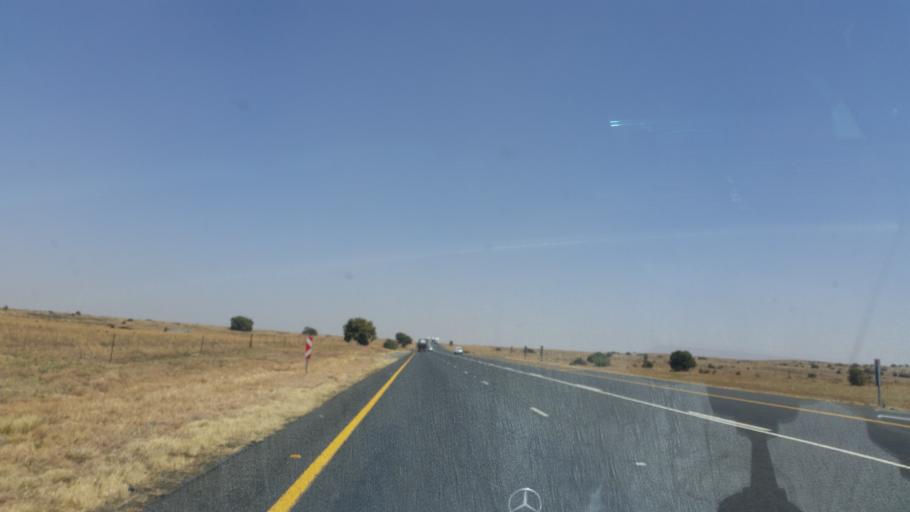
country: ZA
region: Orange Free State
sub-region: Lejweleputswa District Municipality
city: Winburg
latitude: -28.7027
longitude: 26.7959
